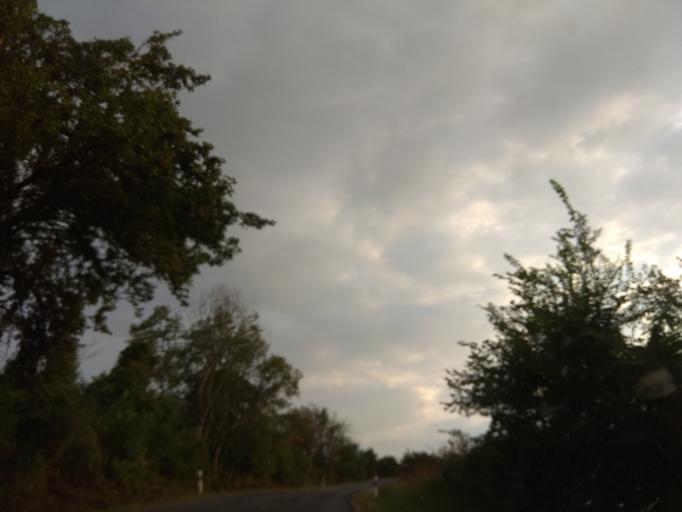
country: HU
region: Borsod-Abauj-Zemplen
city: Malyi
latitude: 48.0404
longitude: 20.7865
